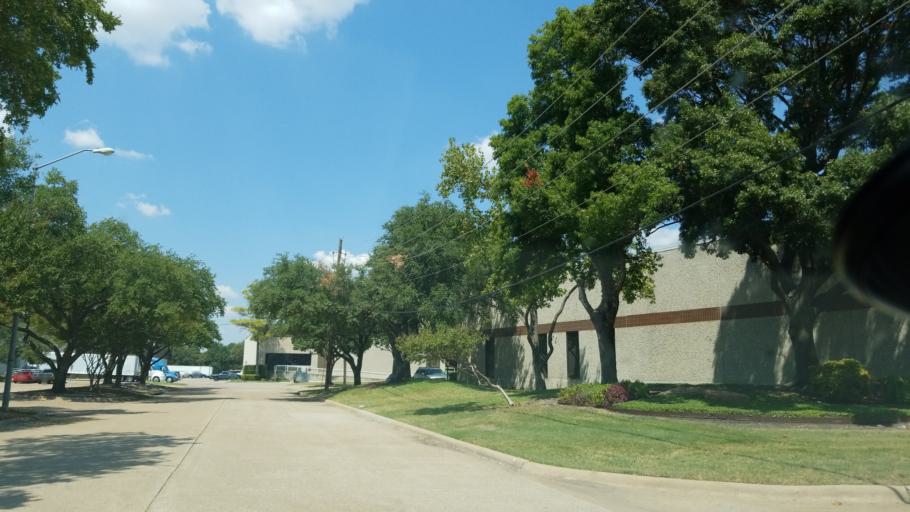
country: US
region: Texas
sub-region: Dallas County
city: Richardson
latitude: 32.8922
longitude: -96.7073
